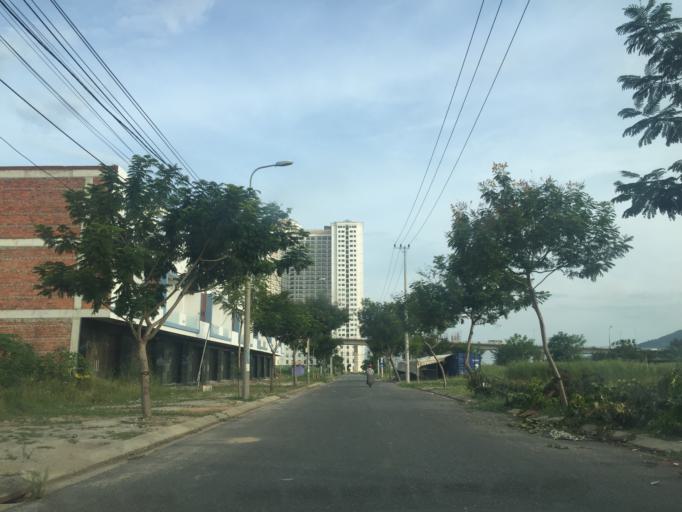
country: VN
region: Da Nang
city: Da Nang
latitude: 16.0949
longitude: 108.2266
